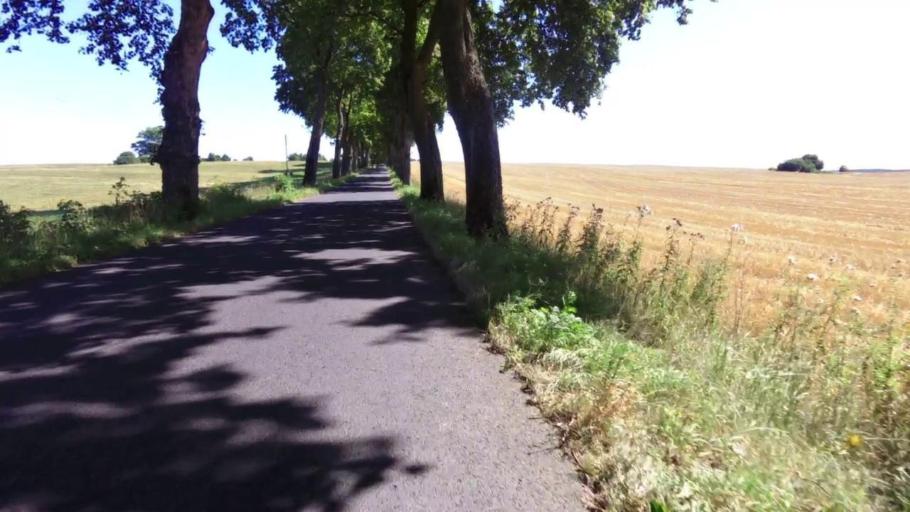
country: PL
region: West Pomeranian Voivodeship
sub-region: Powiat drawski
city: Czaplinek
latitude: 53.5608
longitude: 16.2788
